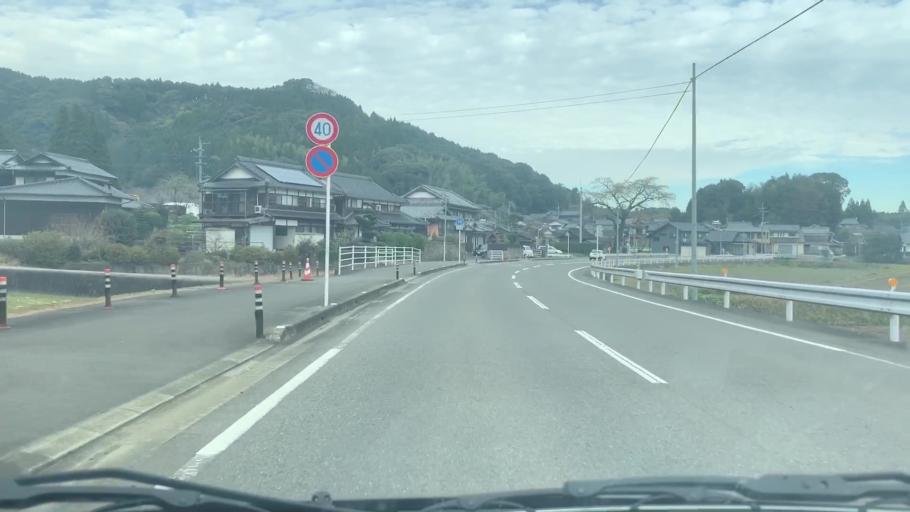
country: JP
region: Saga Prefecture
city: Takeocho-takeo
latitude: 33.1995
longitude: 129.9609
